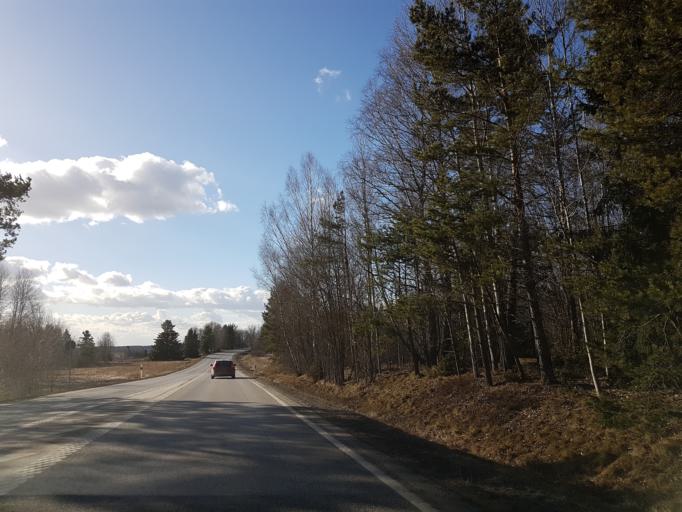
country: SE
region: Stockholm
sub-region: Norrtalje Kommun
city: Norrtalje
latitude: 59.7329
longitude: 18.5584
